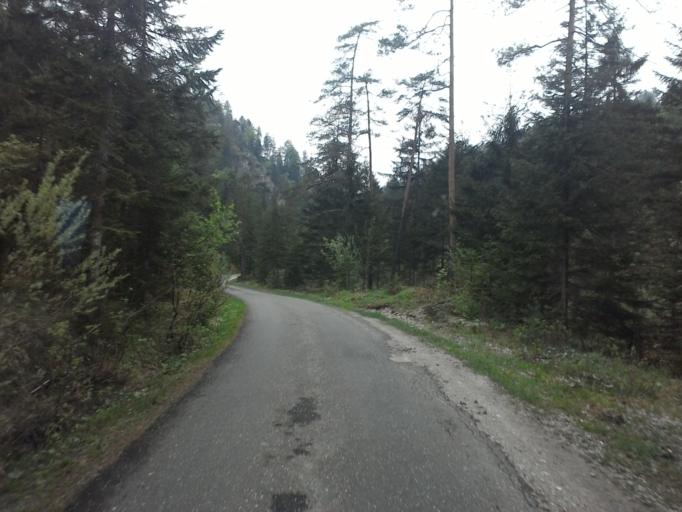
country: AT
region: Styria
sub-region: Politischer Bezirk Liezen
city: Wildalpen
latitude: 47.7014
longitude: 14.9923
